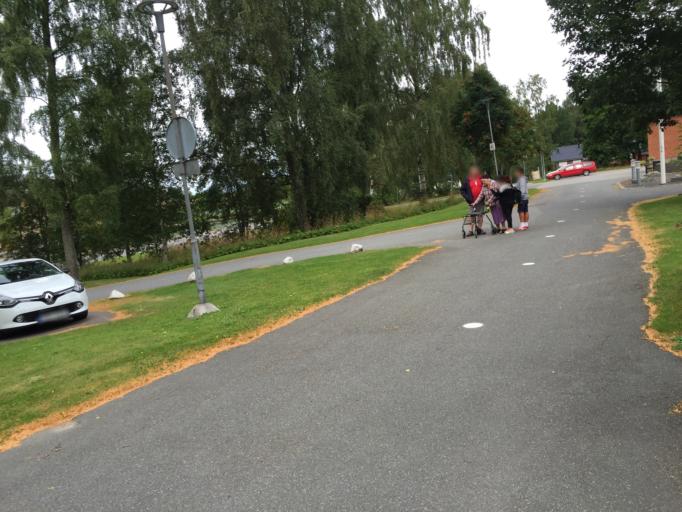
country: SE
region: Skane
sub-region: Hassleholms Kommun
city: Sosdala
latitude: 56.0417
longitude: 13.6771
